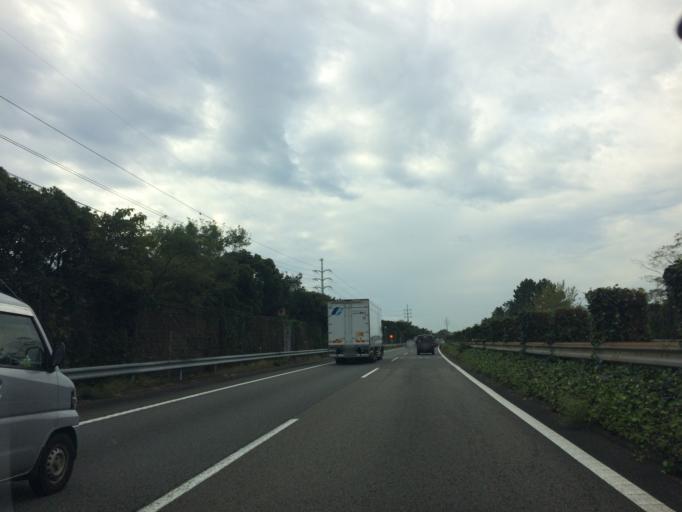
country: JP
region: Shizuoka
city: Fujieda
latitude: 34.8446
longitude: 138.2822
